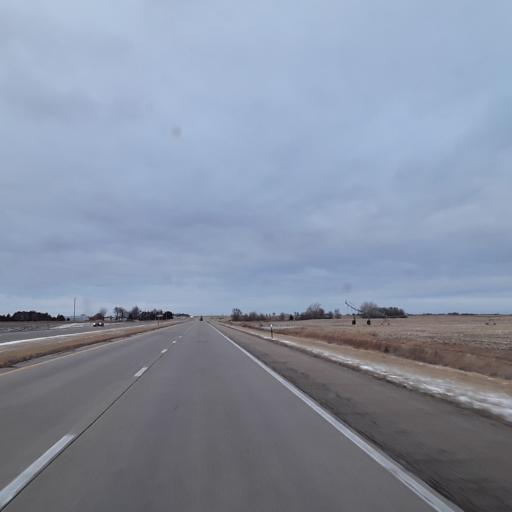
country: US
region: Nebraska
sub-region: Fillmore County
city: Geneva
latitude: 40.6549
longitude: -97.5957
